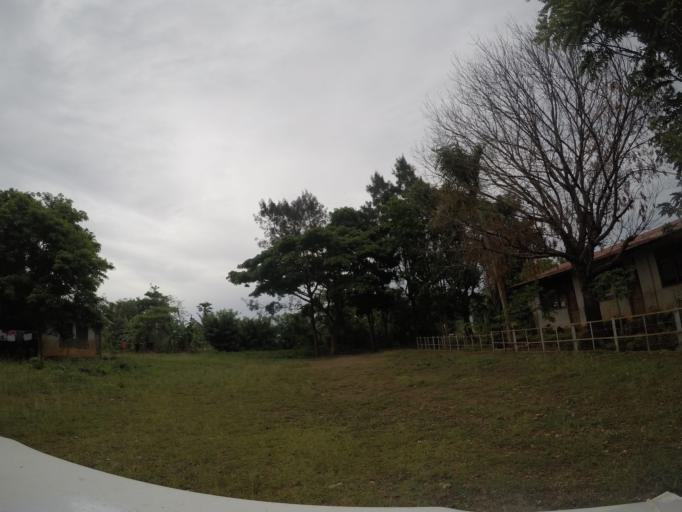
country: TL
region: Lautem
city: Lospalos
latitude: -8.5338
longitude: 127.0000
